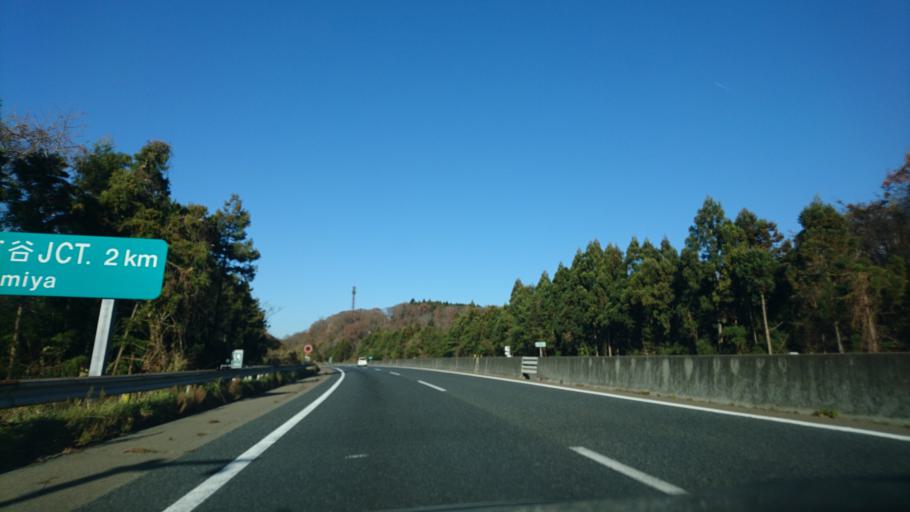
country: JP
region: Miyagi
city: Tomiya
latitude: 38.3535
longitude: 140.8813
